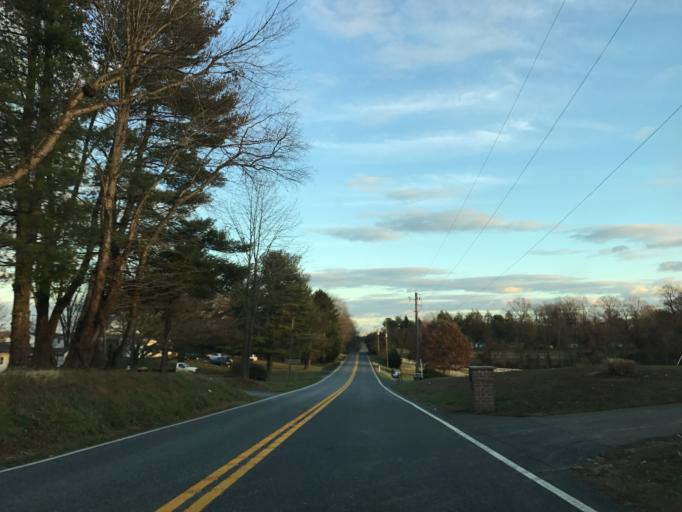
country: US
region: Pennsylvania
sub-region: York County
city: Susquehanna Trails
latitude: 39.7085
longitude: -76.2624
